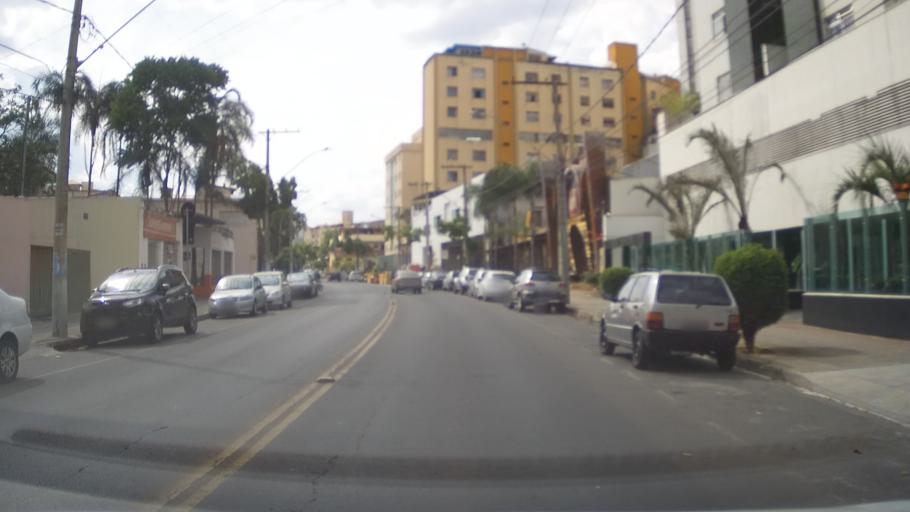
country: BR
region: Minas Gerais
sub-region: Belo Horizonte
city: Belo Horizonte
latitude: -19.9056
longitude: -43.9158
